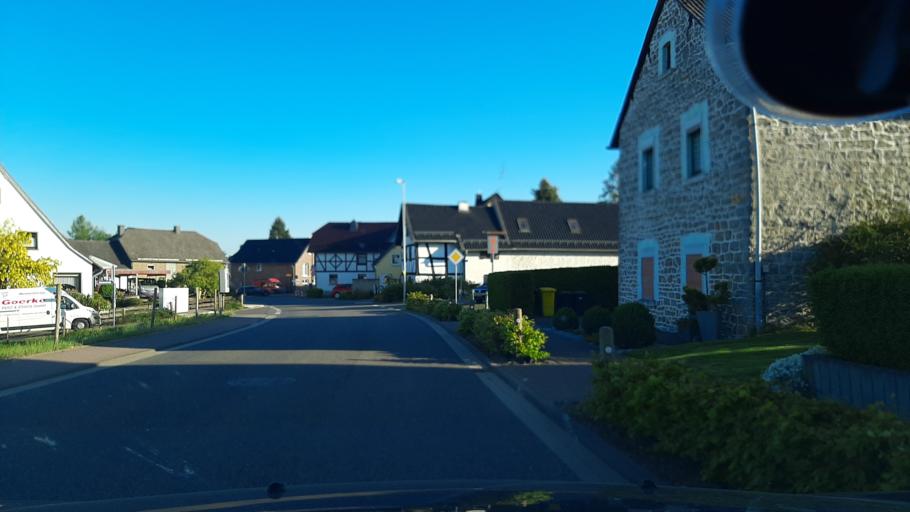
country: DE
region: Rheinland-Pfalz
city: Ohlenhard
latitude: 50.4751
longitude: 6.7135
